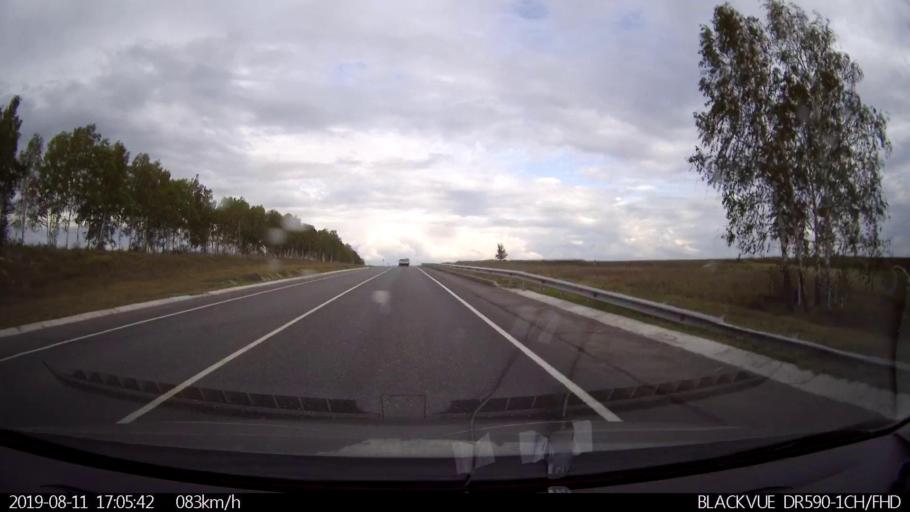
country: RU
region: Ulyanovsk
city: Mayna
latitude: 54.2972
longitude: 47.7915
